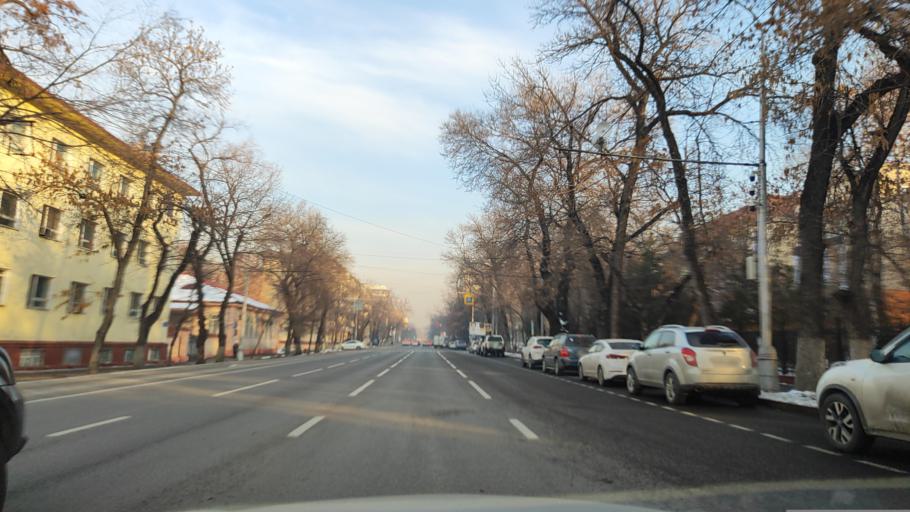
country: KZ
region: Almaty Qalasy
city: Almaty
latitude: 43.2502
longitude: 76.9530
